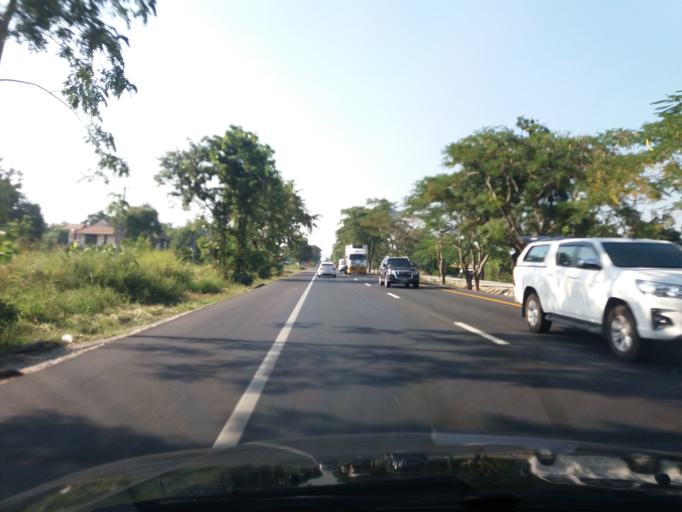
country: TH
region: Nakhon Sawan
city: Kao Liao
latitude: 15.7791
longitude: 99.9767
